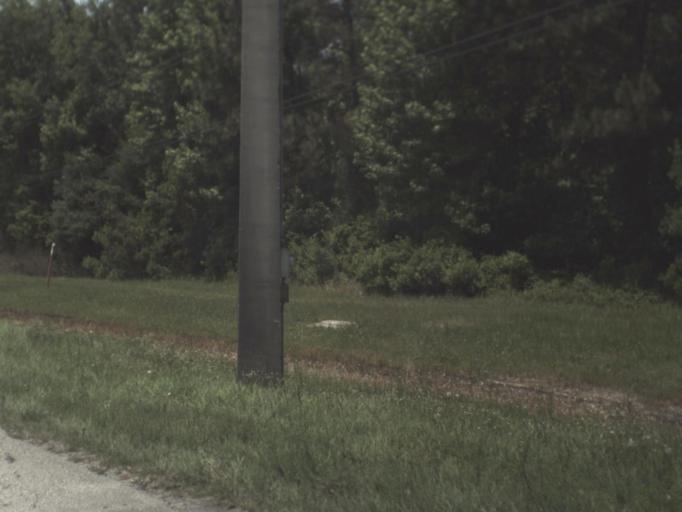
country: US
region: Florida
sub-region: Duval County
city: Baldwin
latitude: 30.2002
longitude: -82.0153
